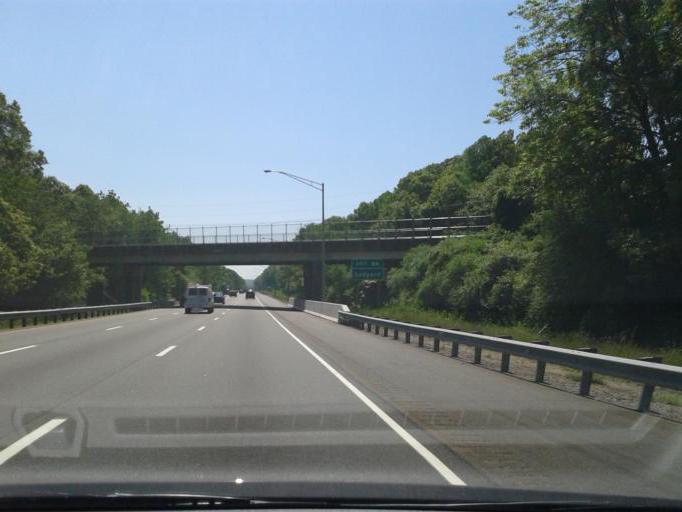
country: US
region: Connecticut
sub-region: New London County
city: Poquonock Bridge
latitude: 41.3687
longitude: -72.0061
